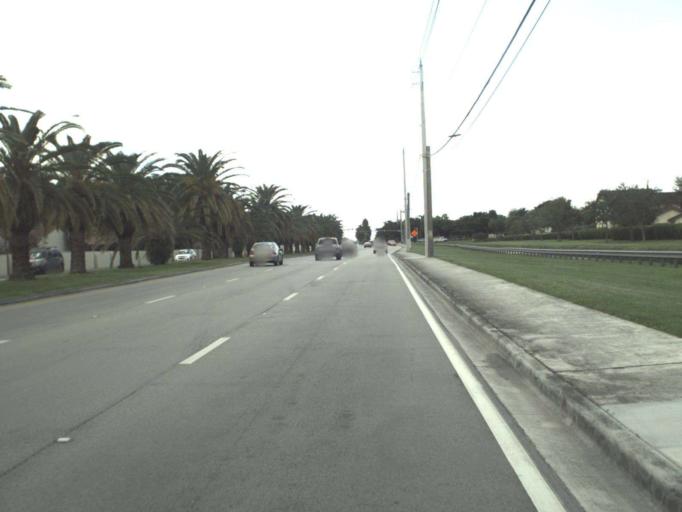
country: US
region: Florida
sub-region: Miami-Dade County
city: The Crossings
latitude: 25.6744
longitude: -80.4166
